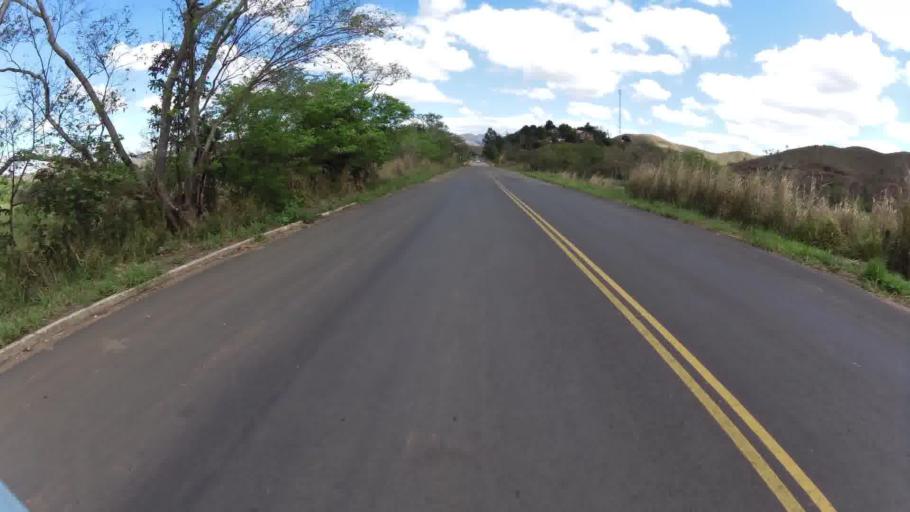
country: BR
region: Rio de Janeiro
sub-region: Itaperuna
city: Itaperuna
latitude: -21.2718
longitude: -41.7824
